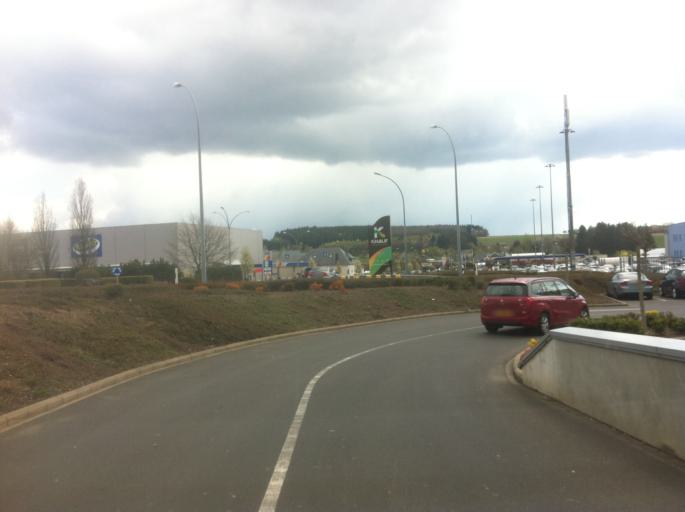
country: LU
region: Diekirch
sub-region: Canton de Wiltz
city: Winseler
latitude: 49.9646
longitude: 5.8581
